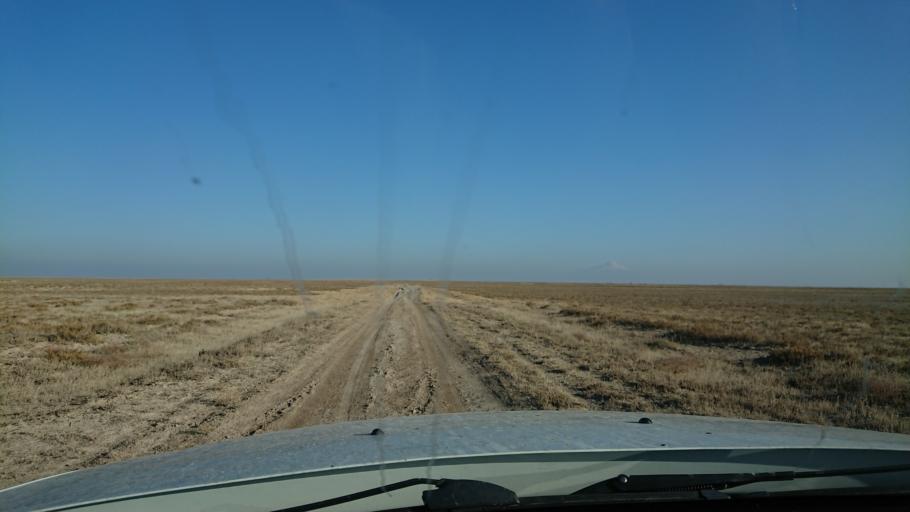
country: TR
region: Aksaray
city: Eskil
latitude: 38.4077
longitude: 33.5658
